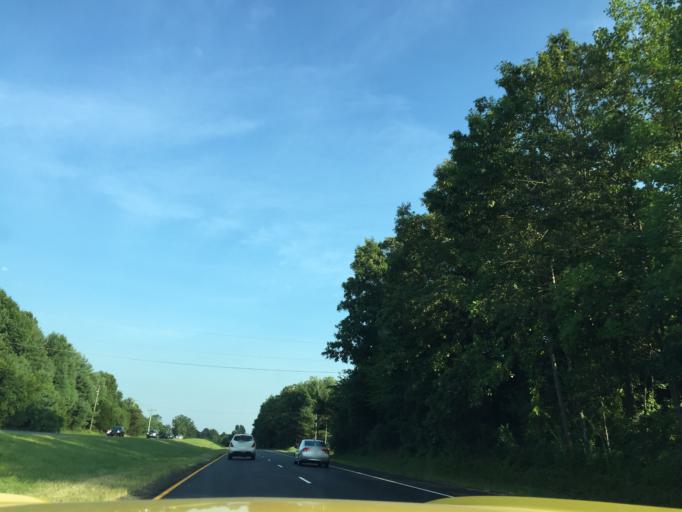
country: US
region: Virginia
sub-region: Fairfax County
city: Reston
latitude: 38.9840
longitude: -77.3223
